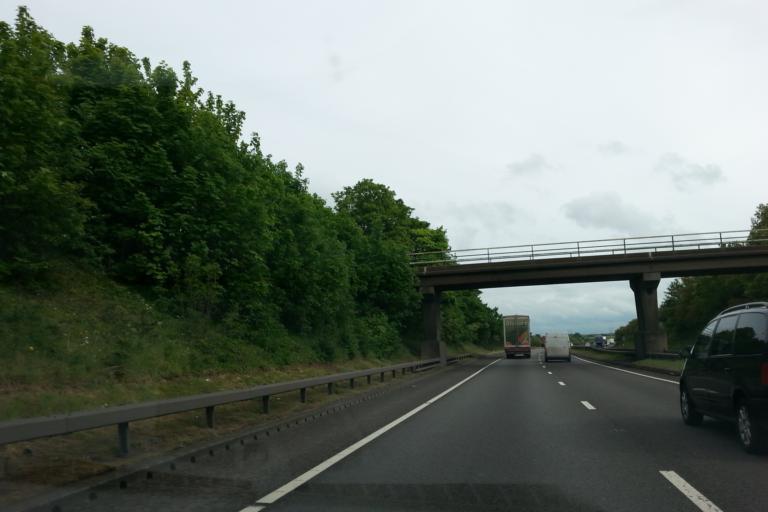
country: GB
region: England
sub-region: Nottinghamshire
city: Bircotes
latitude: 53.3844
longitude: -1.0575
